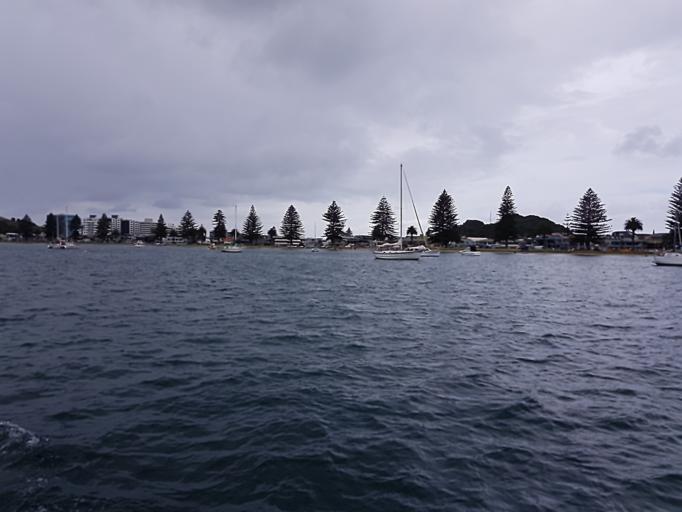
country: NZ
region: Bay of Plenty
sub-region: Tauranga City
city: Tauranga
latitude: -37.6400
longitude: 176.1789
